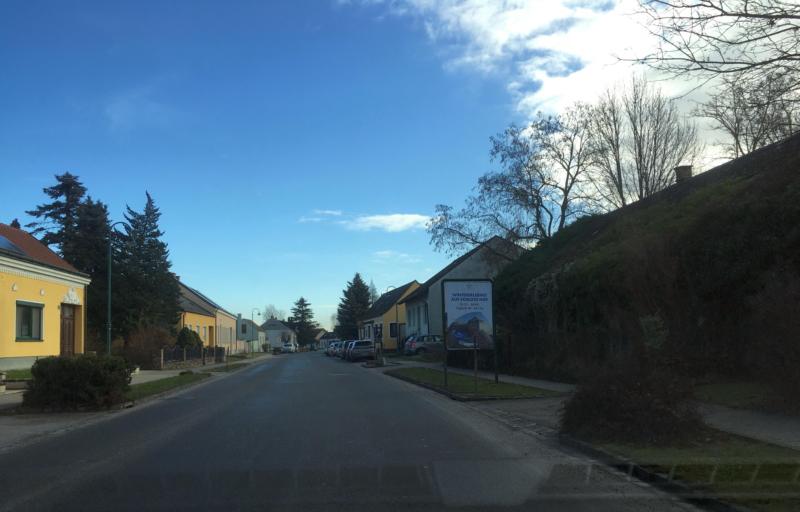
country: AT
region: Lower Austria
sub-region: Politischer Bezirk Ganserndorf
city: Eckartsau
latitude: 48.1450
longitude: 16.7981
